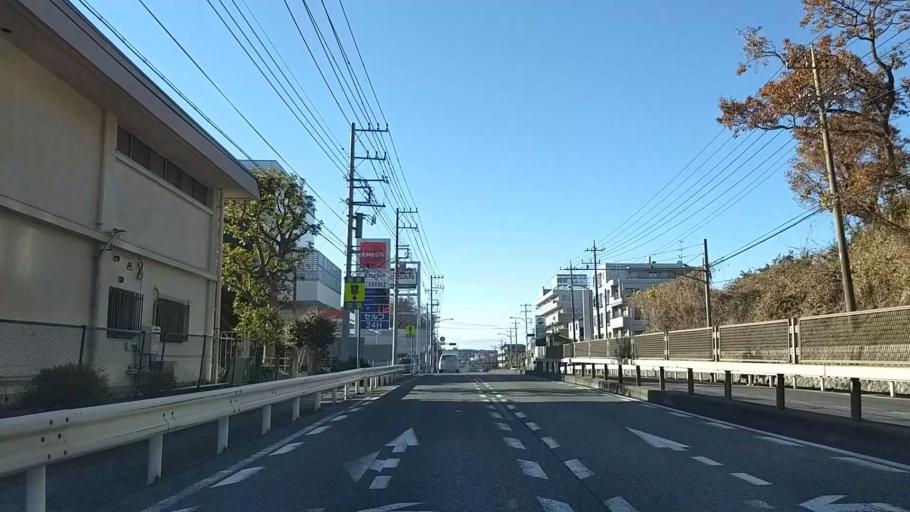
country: JP
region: Tokyo
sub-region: Machida-shi
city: Machida
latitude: 35.5383
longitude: 139.5125
